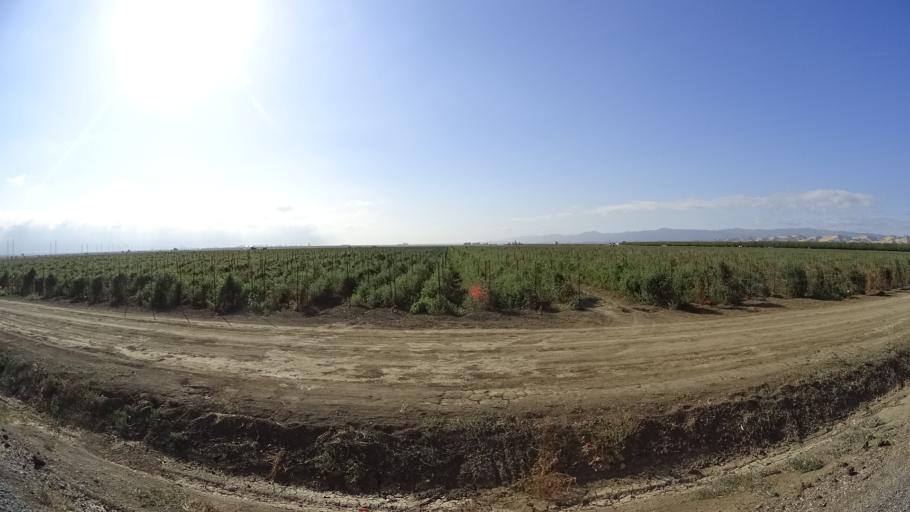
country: US
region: California
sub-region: Yolo County
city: Esparto
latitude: 38.7810
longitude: -122.0225
